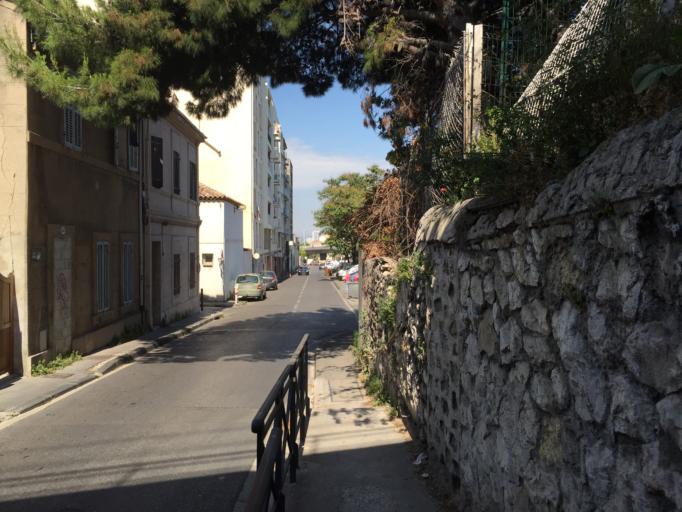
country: FR
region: Provence-Alpes-Cote d'Azur
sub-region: Departement des Bouches-du-Rhone
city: Marseille 04
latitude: 43.3142
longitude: 5.3930
